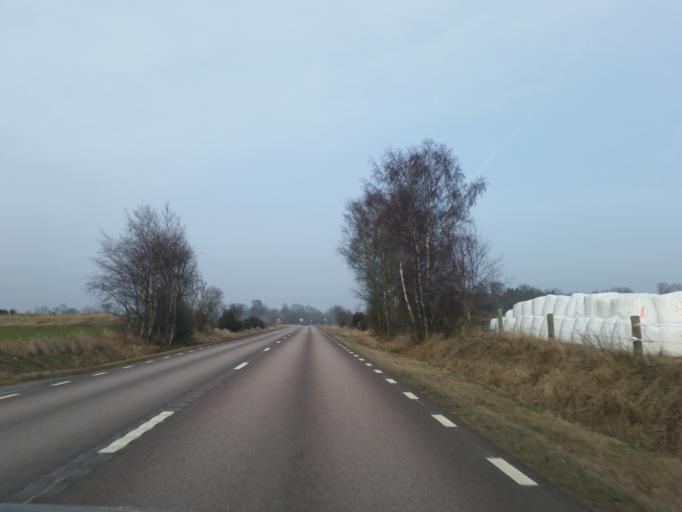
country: SE
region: Kalmar
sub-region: Borgholms Kommun
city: Borgholm
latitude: 57.1419
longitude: 16.9998
